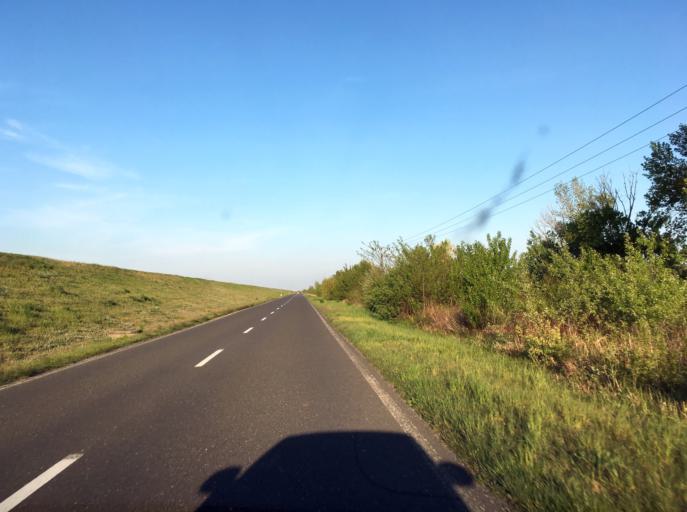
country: SK
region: Trnavsky
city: Samorin
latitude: 47.9967
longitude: 17.2868
